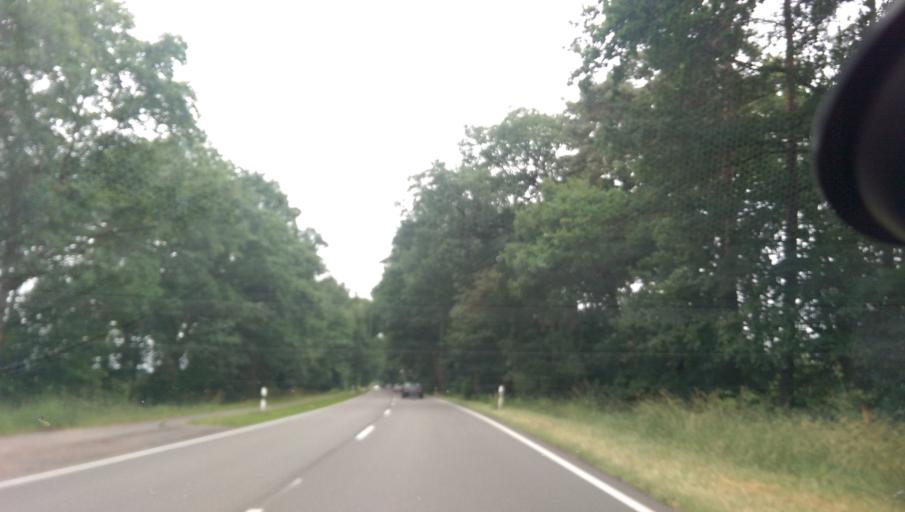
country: DE
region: Lower Saxony
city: Botersen
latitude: 53.1641
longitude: 9.3179
